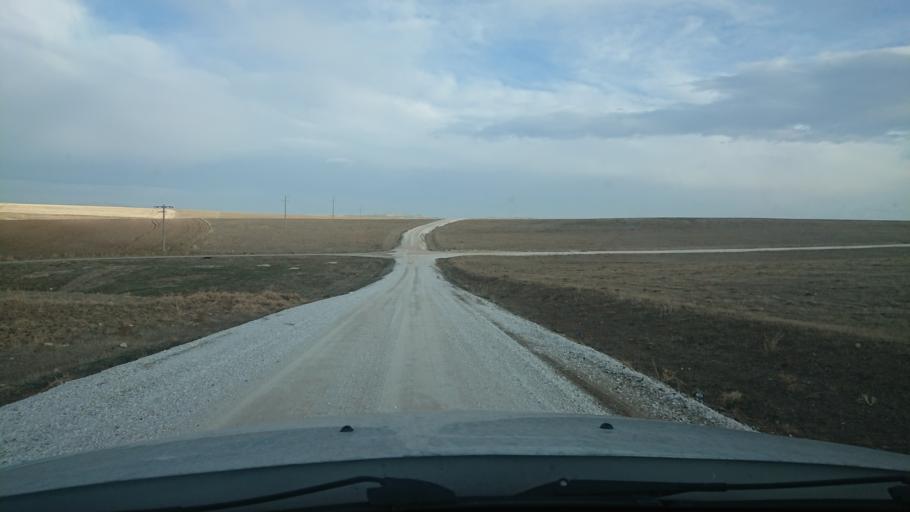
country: TR
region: Aksaray
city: Agacoren
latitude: 38.7368
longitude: 33.8695
